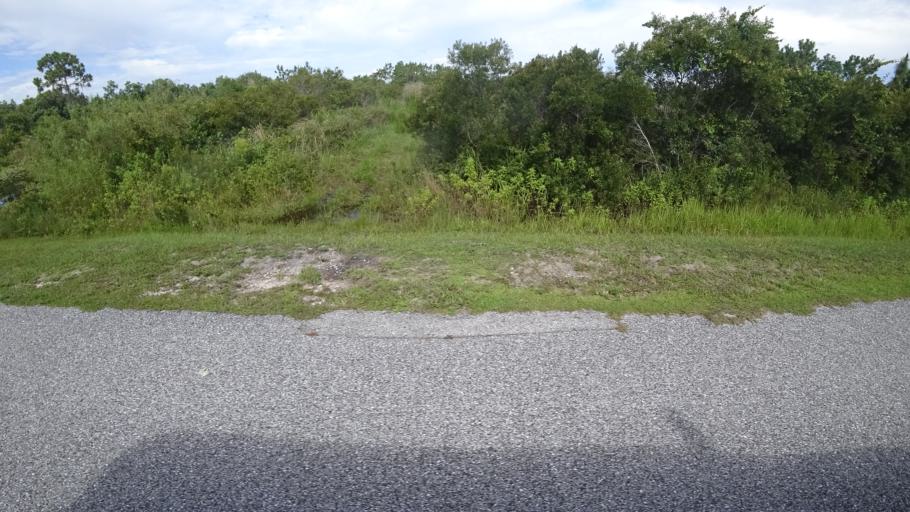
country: US
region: Florida
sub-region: Sarasota County
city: Lake Sarasota
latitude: 27.3905
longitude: -82.2733
